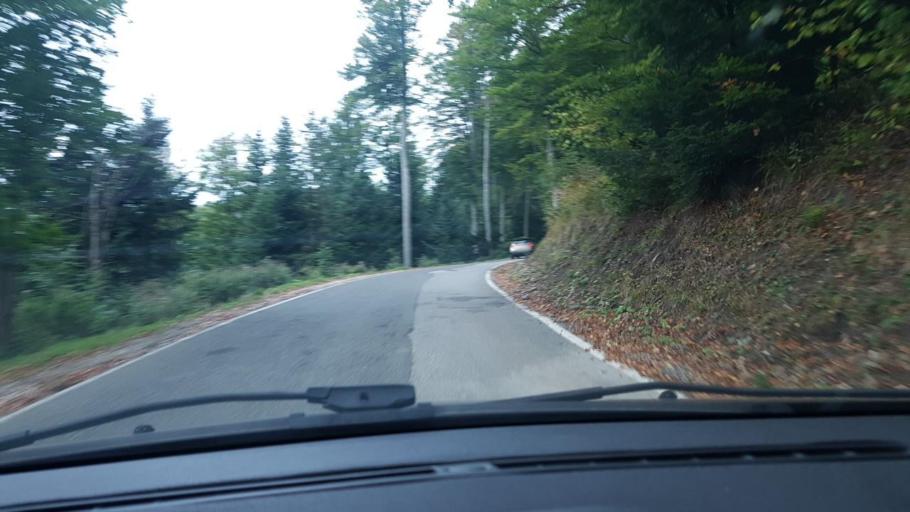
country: HR
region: Grad Zagreb
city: Kasina
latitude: 45.8951
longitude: 15.9504
